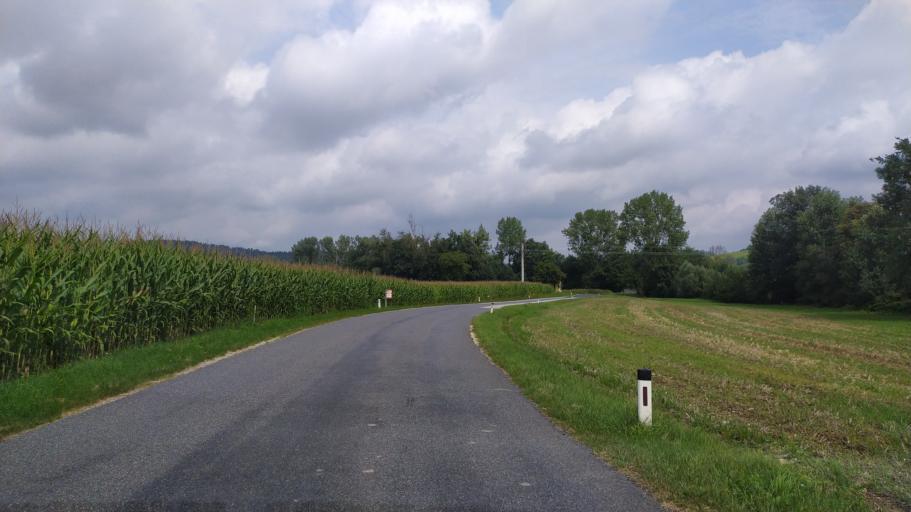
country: AT
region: Upper Austria
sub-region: Politischer Bezirk Perg
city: Bad Kreuzen
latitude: 48.2018
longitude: 14.7841
